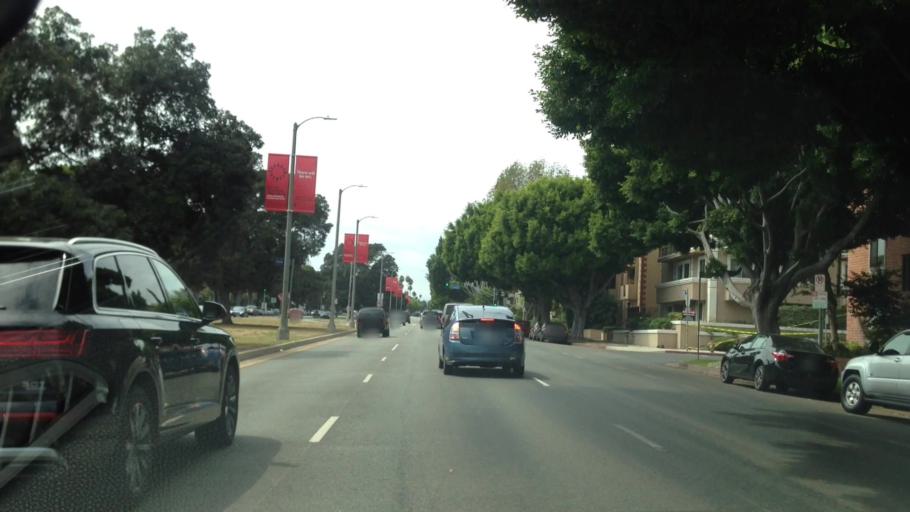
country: US
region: California
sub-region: Los Angeles County
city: Beverly Hills
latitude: 34.0723
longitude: -118.3853
